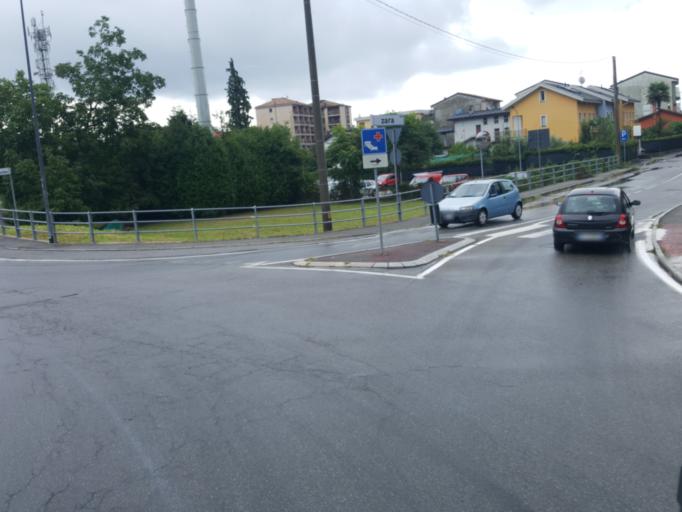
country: IT
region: Piedmont
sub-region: Provincia Verbano-Cusio-Ossola
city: Verbania
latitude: 45.9296
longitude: 8.5474
